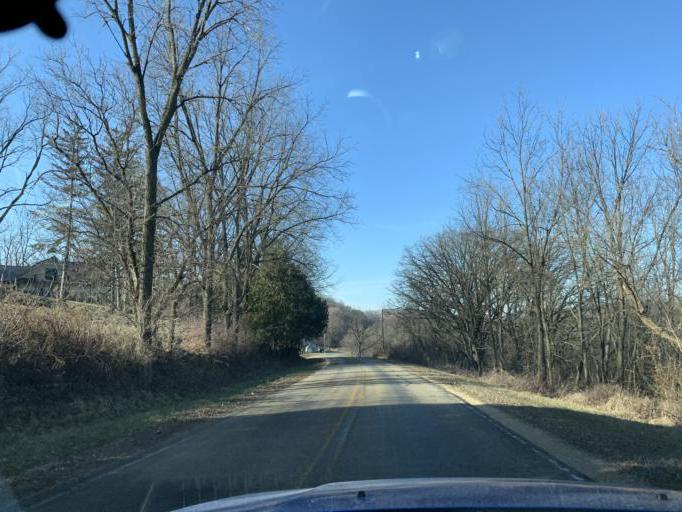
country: US
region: Wisconsin
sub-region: Iowa County
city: Barneveld
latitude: 42.8445
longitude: -89.9316
